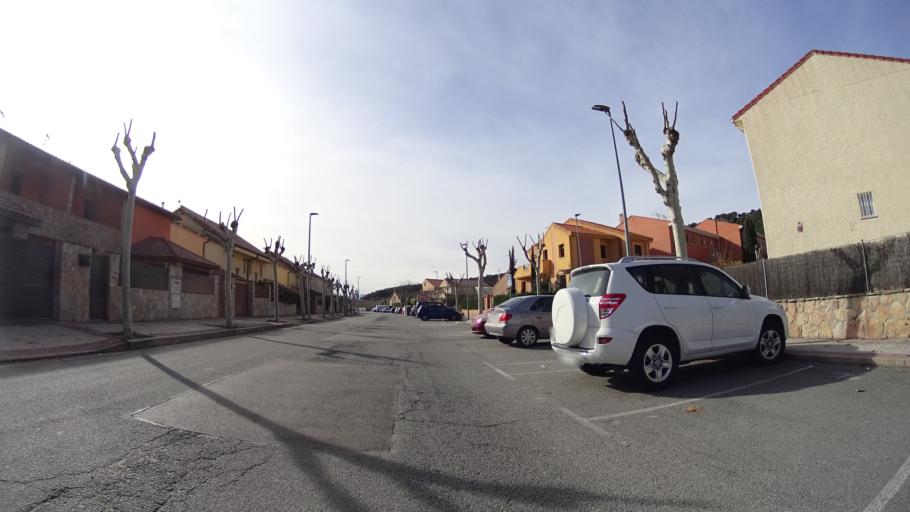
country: ES
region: Madrid
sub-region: Provincia de Madrid
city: Moralzarzal
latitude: 40.6765
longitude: -3.9750
